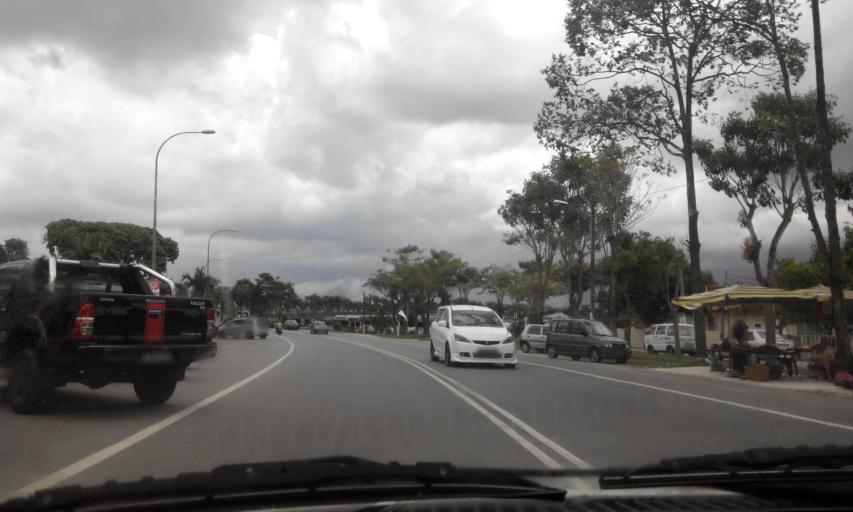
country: MY
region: Perak
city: Parit Buntar
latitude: 5.1135
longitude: 100.4877
